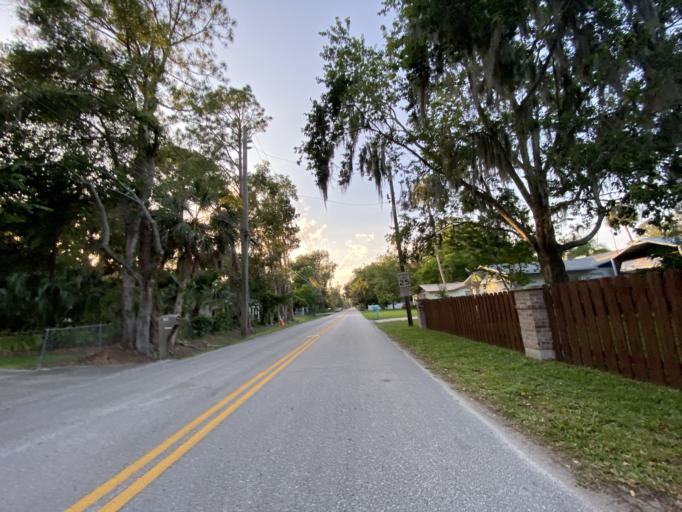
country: US
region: Florida
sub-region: Volusia County
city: Port Orange
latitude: 29.1322
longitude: -81.0053
